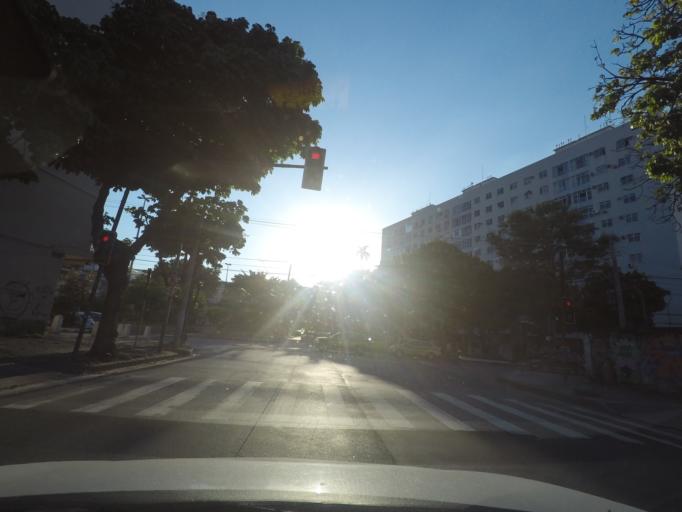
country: BR
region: Rio de Janeiro
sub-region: Rio De Janeiro
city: Rio de Janeiro
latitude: -22.9162
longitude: -43.2121
